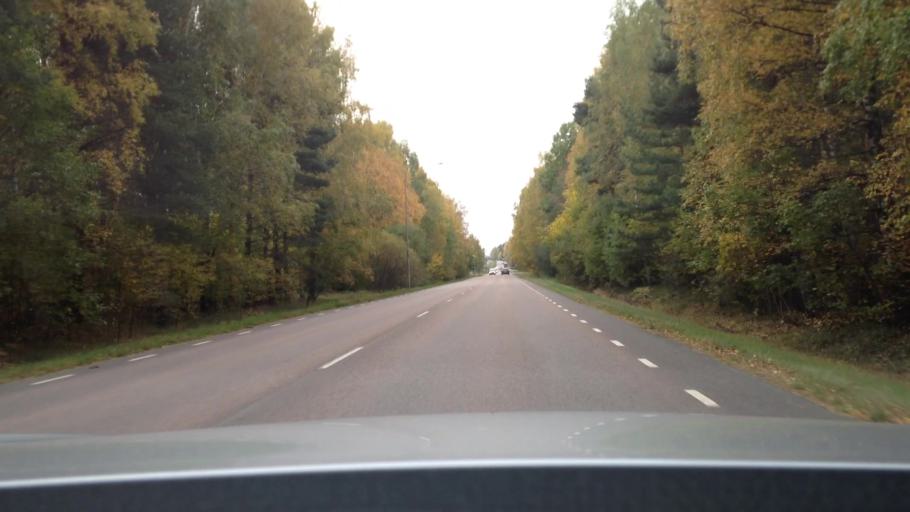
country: SE
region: Vaermland
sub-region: Karlstads Kommun
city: Karlstad
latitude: 59.3745
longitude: 13.4631
